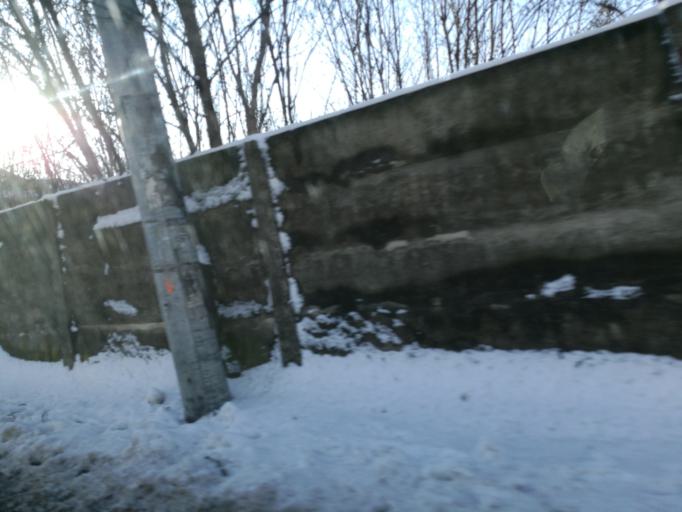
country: RO
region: Ilfov
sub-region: Comuna Tunari
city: Tunari
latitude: 44.5163
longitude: 26.1309
